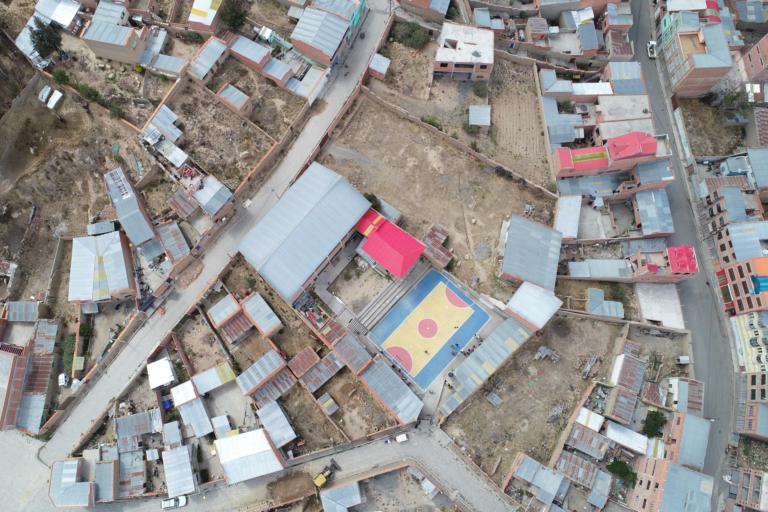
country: BO
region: La Paz
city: Achacachi
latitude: -16.0412
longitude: -68.6841
